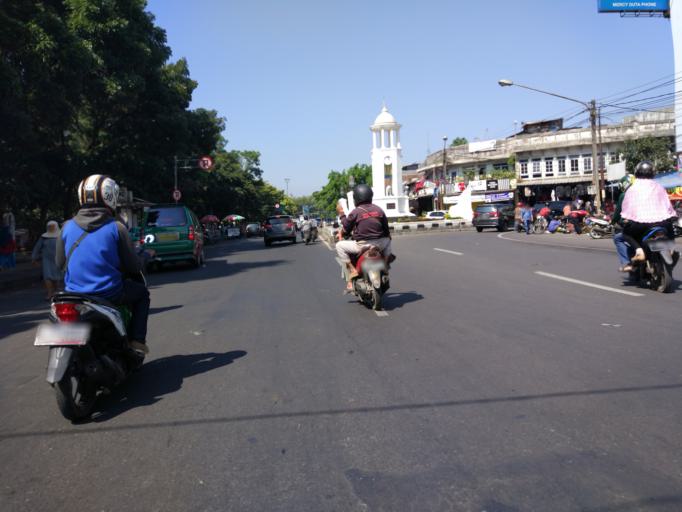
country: ID
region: West Java
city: Bandung
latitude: -6.9351
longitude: 107.6032
